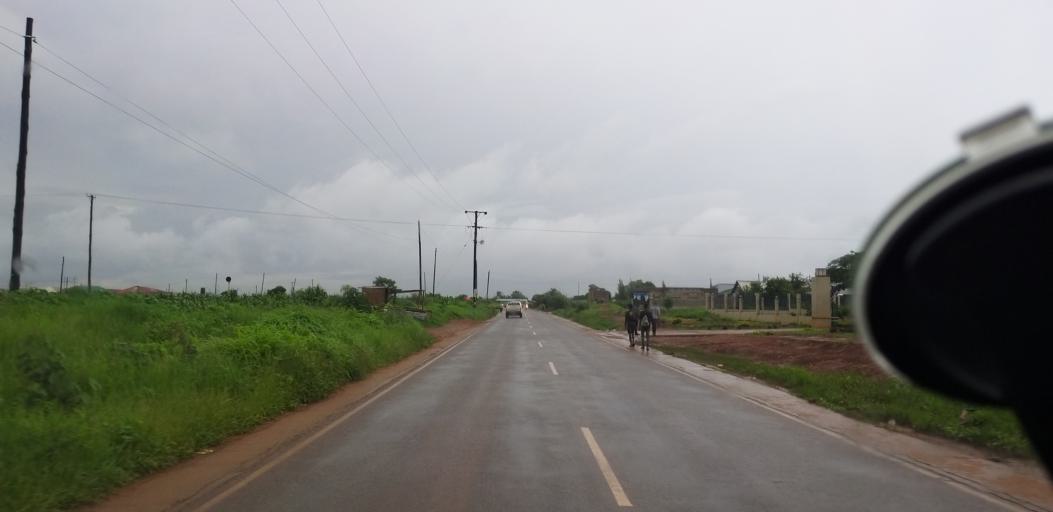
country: ZM
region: Lusaka
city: Lusaka
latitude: -15.5182
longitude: 28.2976
